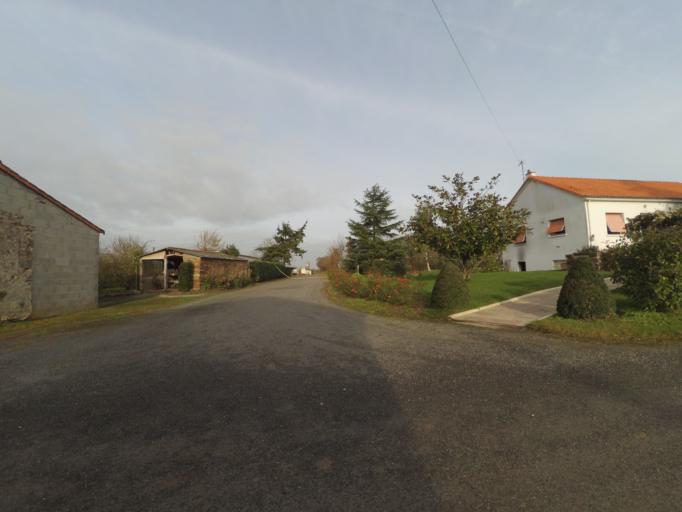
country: FR
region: Pays de la Loire
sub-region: Departement de la Loire-Atlantique
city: Vieillevigne
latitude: 46.9882
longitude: -1.4012
